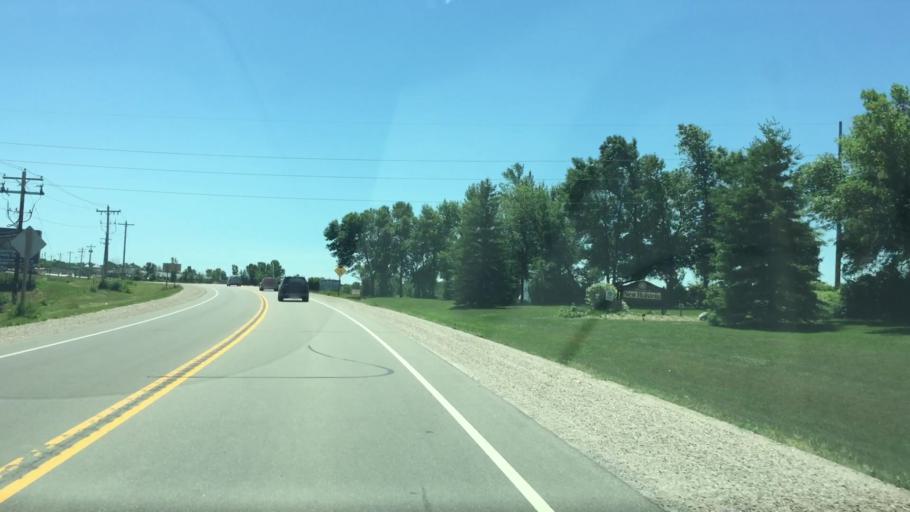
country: US
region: Wisconsin
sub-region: Calumet County
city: New Holstein
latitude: 43.9613
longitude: -88.1121
